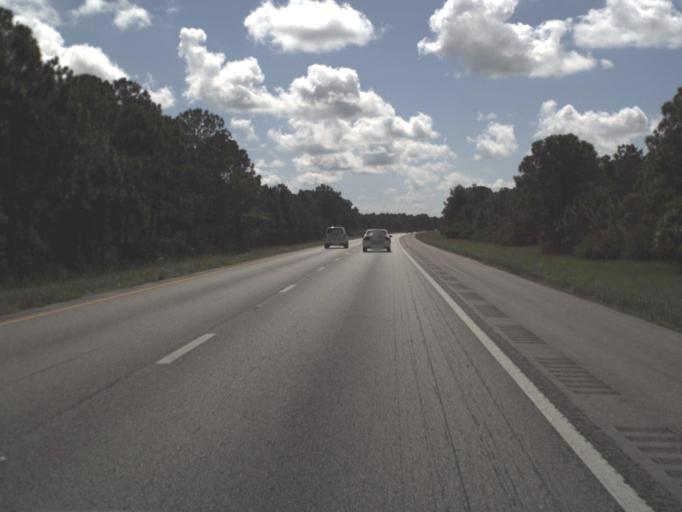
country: US
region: Florida
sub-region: Lee County
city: Suncoast Estates
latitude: 26.8000
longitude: -81.9175
